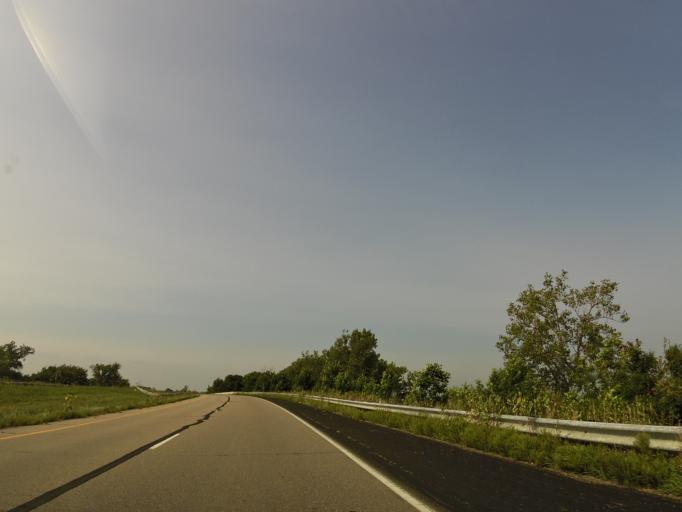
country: US
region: Minnesota
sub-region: Carver County
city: Norwood (historical)
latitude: 44.7717
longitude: -93.9518
